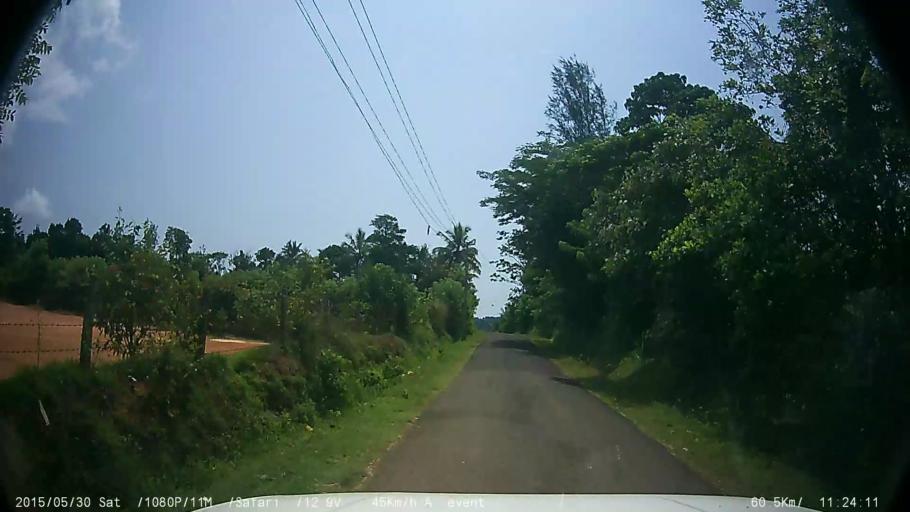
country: IN
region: Kerala
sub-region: Wayanad
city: Panamaram
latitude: 11.8047
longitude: 76.0286
